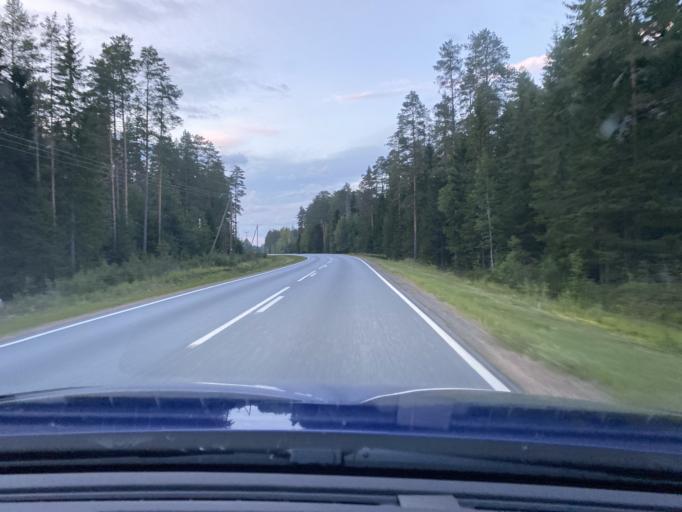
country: FI
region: Satakunta
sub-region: Pohjois-Satakunta
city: Honkajoki
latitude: 62.1585
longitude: 22.2666
